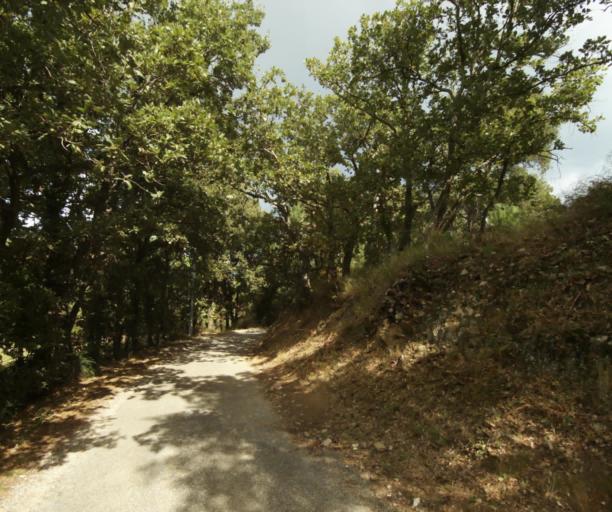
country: FR
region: Languedoc-Roussillon
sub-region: Departement des Pyrenees-Orientales
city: Argelers
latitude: 42.5401
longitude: 3.0124
